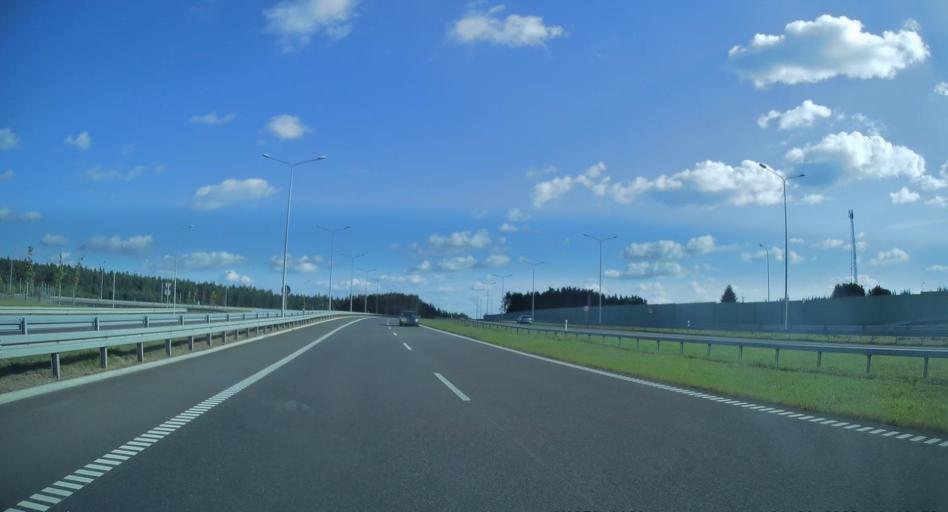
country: PL
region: Masovian Voivodeship
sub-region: Powiat szydlowiecki
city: Oronsko
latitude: 51.3307
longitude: 21.0162
